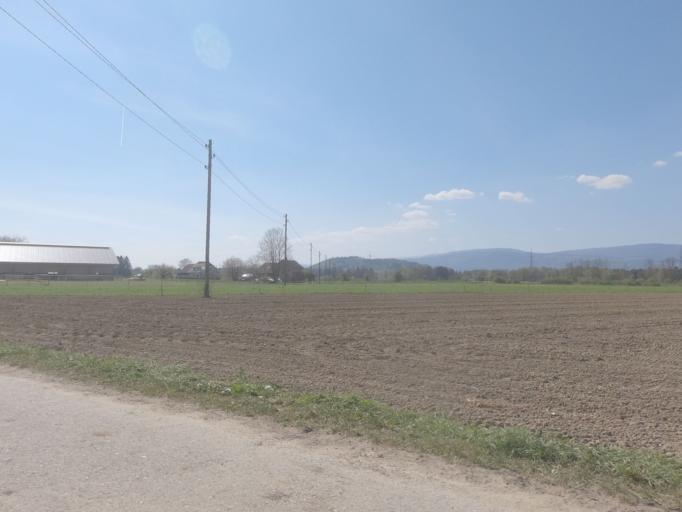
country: CH
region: Bern
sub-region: Biel/Bienne District
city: Orpund
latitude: 47.1112
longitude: 7.3352
